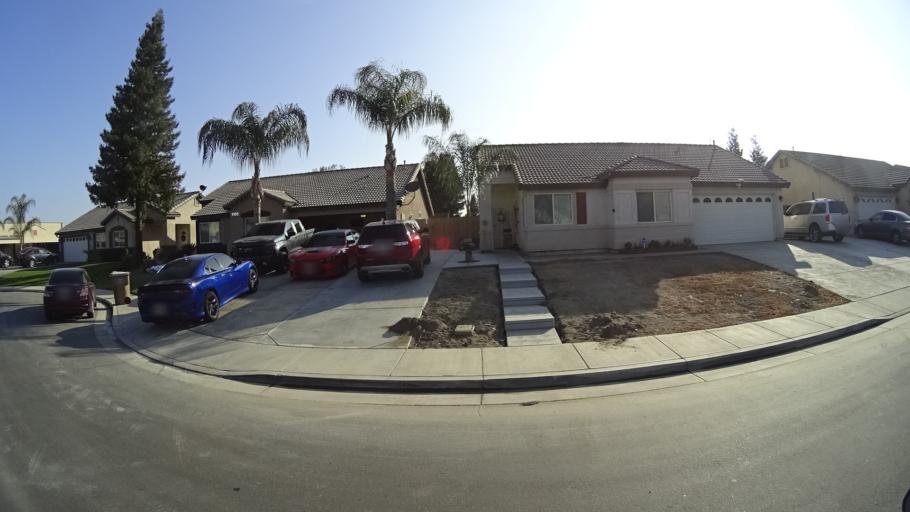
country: US
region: California
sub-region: Kern County
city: Greenfield
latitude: 35.2834
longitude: -119.0146
